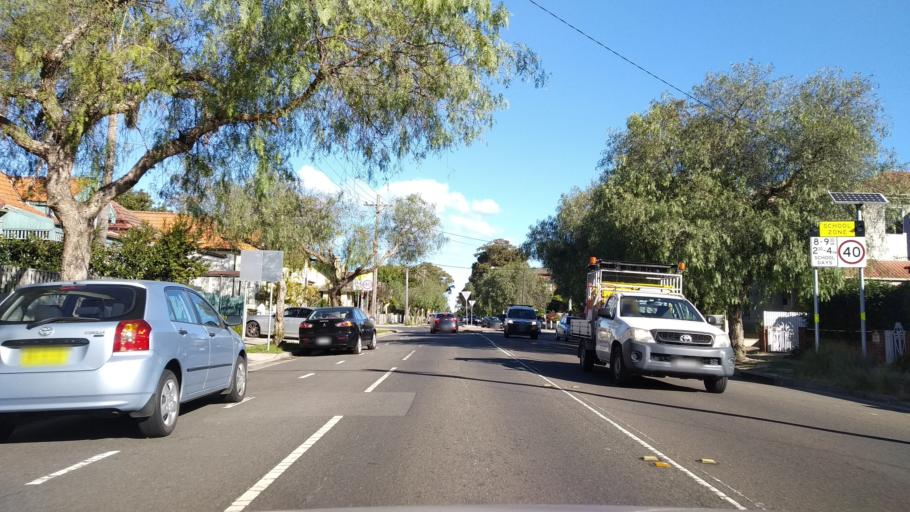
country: AU
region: New South Wales
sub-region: Randwick
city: Kensington
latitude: -33.9076
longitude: 151.2258
